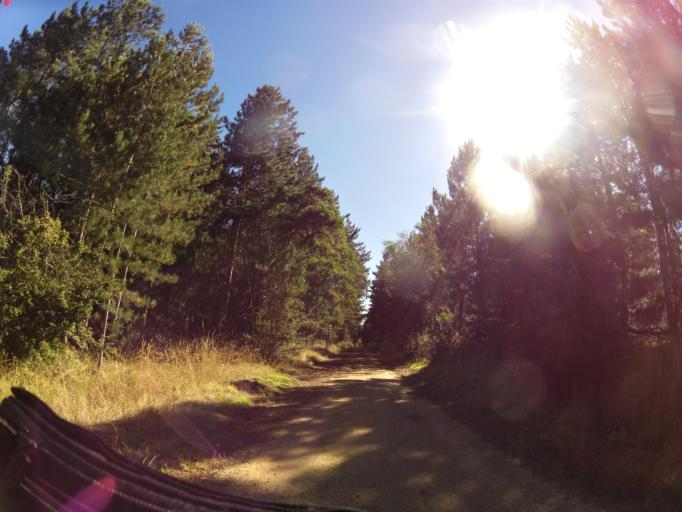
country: AU
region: Victoria
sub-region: Ballarat North
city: Delacombe
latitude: -37.6808
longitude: 143.4344
